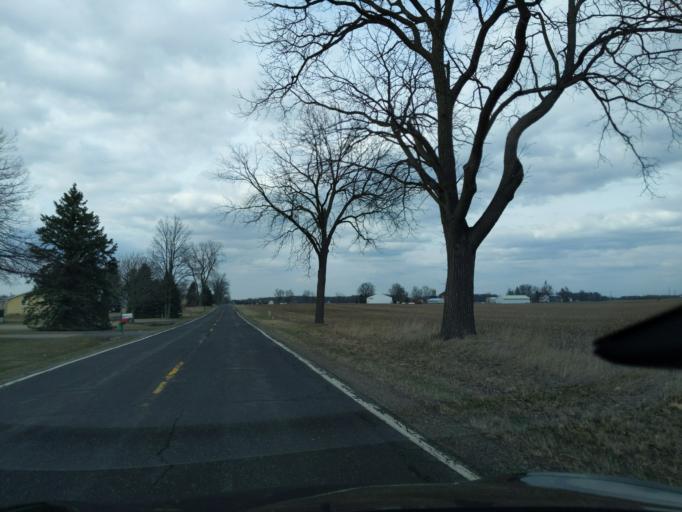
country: US
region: Michigan
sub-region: Ingham County
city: Mason
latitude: 42.5769
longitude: -84.4834
